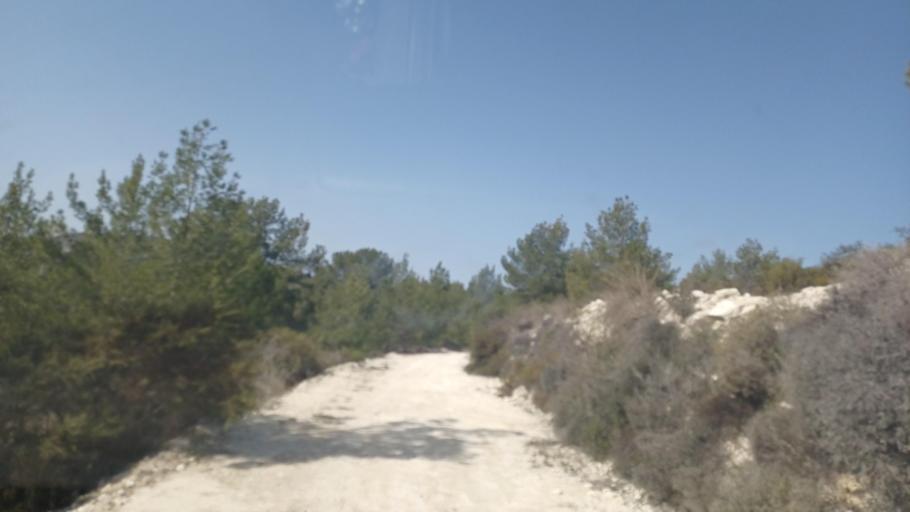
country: CY
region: Limassol
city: Pachna
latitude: 34.8849
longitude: 32.7210
